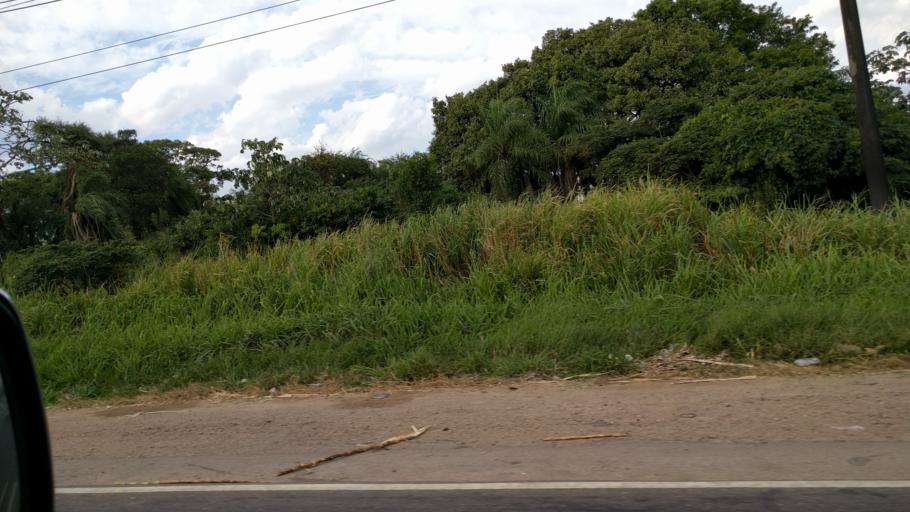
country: BO
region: Santa Cruz
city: Warnes
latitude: -17.5491
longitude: -63.1601
